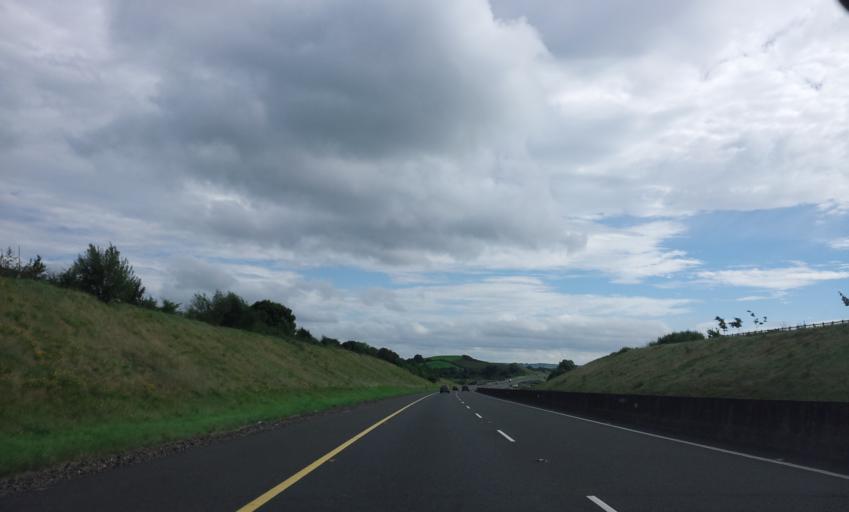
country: IE
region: Munster
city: Ballina
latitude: 52.7865
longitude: -8.3629
